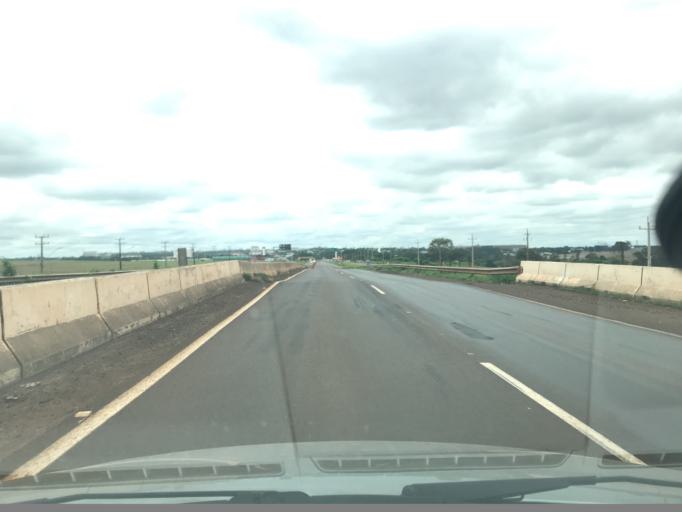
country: BR
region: Parana
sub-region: Paicandu
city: Paicandu
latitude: -23.4572
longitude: -52.0218
